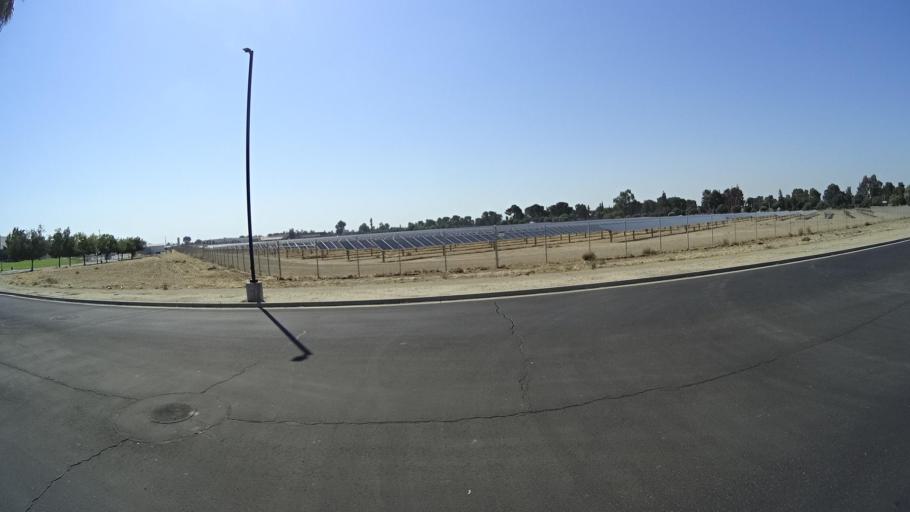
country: US
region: California
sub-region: Fresno County
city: Tarpey Village
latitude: 36.7822
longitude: -119.7089
